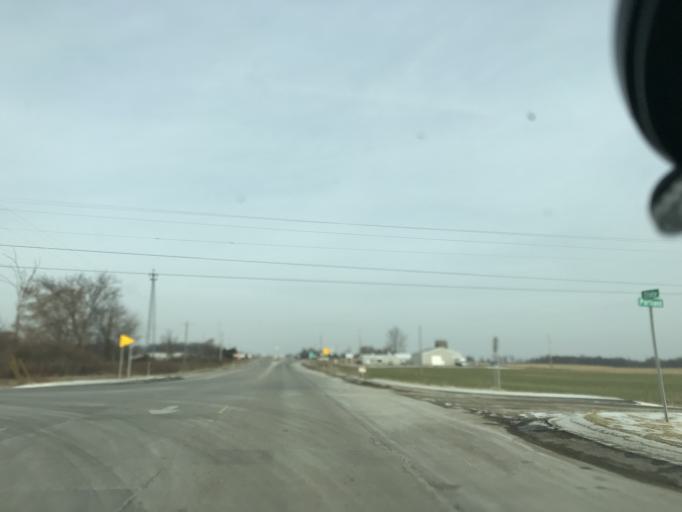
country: US
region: Michigan
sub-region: Ionia County
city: Lake Odessa
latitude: 42.8713
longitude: -85.0750
